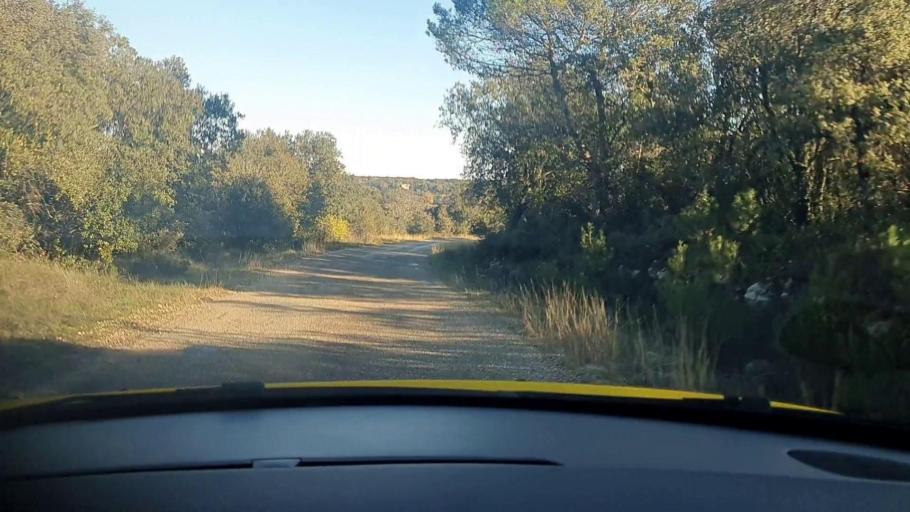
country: FR
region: Languedoc-Roussillon
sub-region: Departement du Gard
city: Goudargues
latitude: 44.1697
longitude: 4.3564
